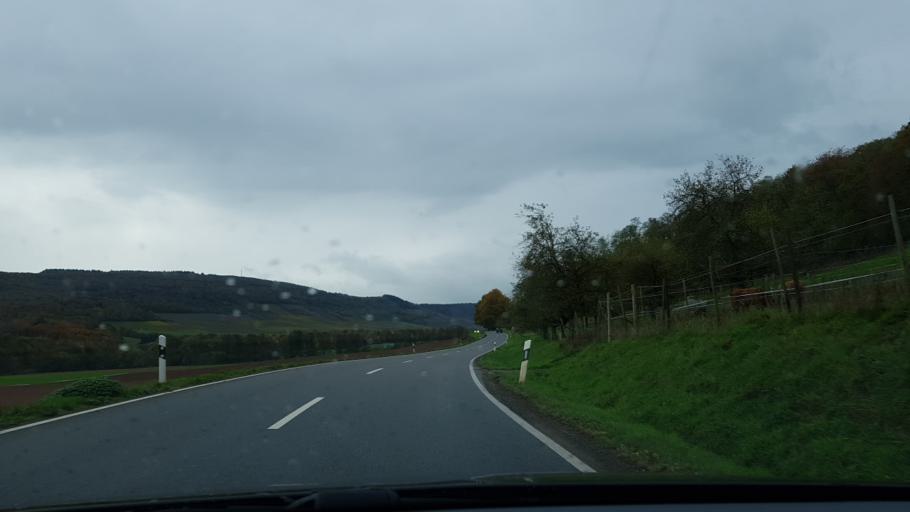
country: DE
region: Rheinland-Pfalz
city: Esch
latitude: 49.8922
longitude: 6.8420
